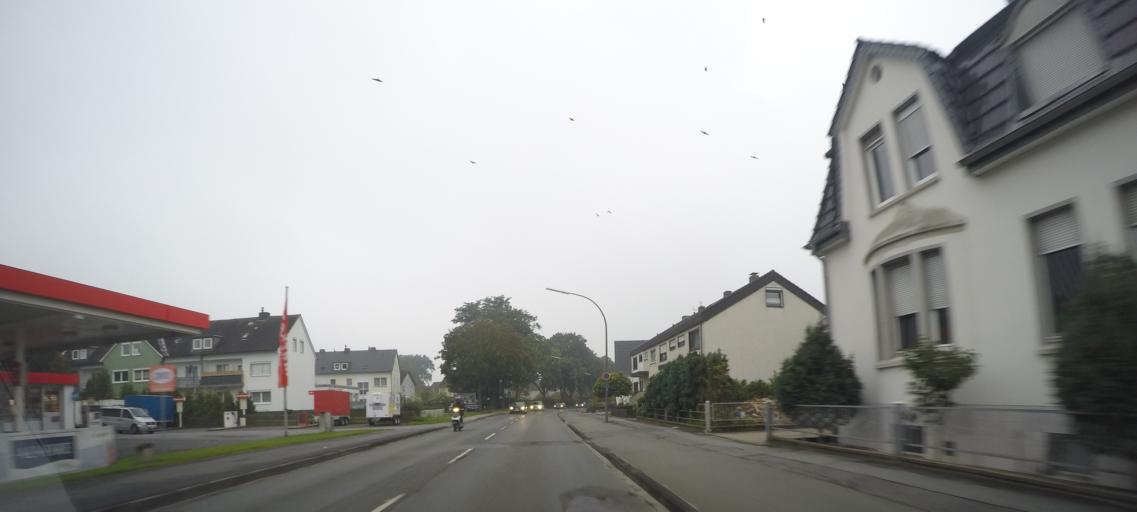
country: DE
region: North Rhine-Westphalia
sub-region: Regierungsbezirk Arnsberg
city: Lippstadt
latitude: 51.6807
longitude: 8.3114
